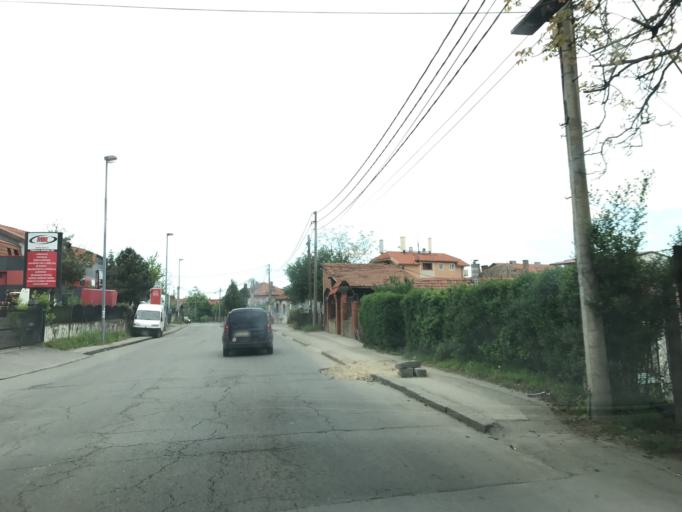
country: RS
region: Central Serbia
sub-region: Belgrade
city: Palilula
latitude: 44.8043
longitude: 20.5183
